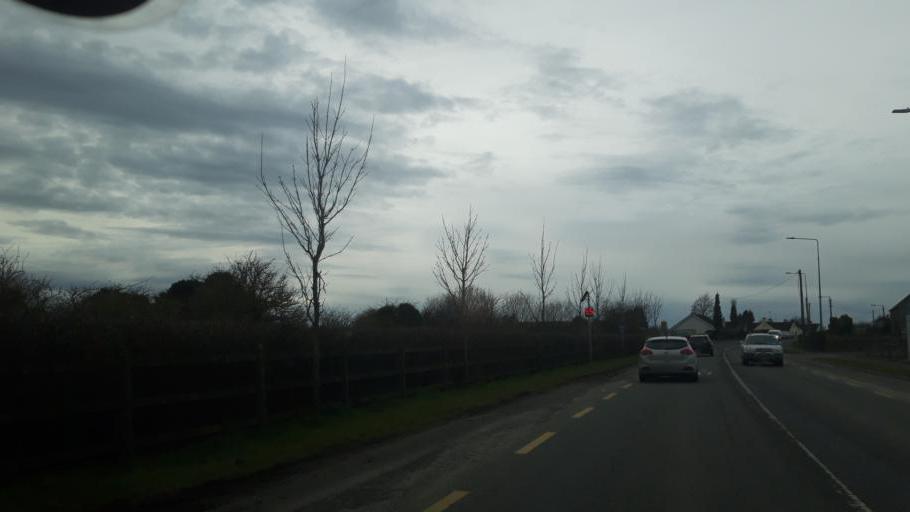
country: IE
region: Leinster
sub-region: Uibh Fhaili
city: Edenderry
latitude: 53.3467
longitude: -7.0326
